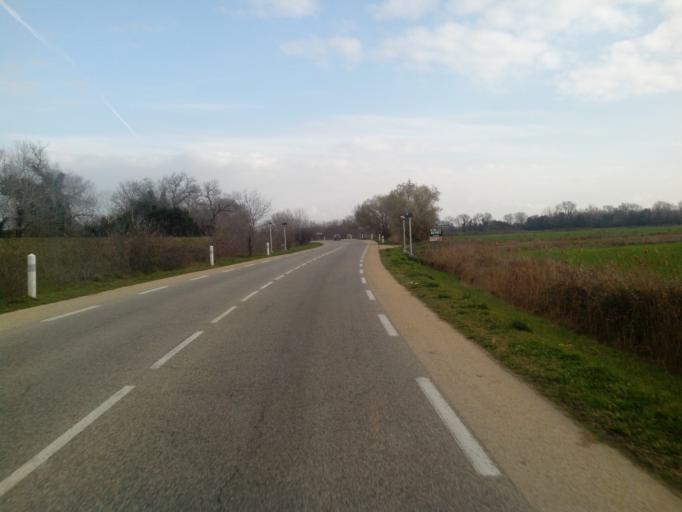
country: FR
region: Languedoc-Roussillon
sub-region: Departement du Gard
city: Saint-Gilles
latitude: 43.5825
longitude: 4.4431
